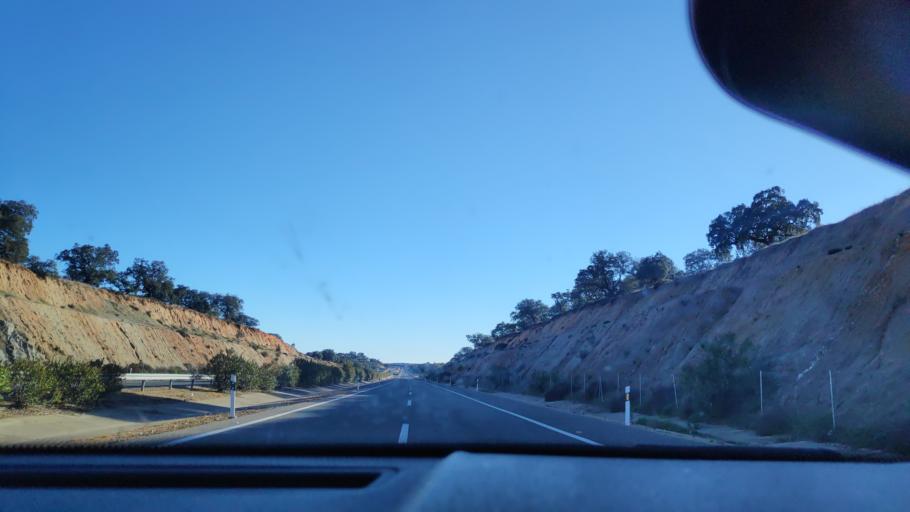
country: ES
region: Andalusia
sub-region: Provincia de Huelva
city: Santa Olalla del Cala
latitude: 37.9643
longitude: -6.2350
